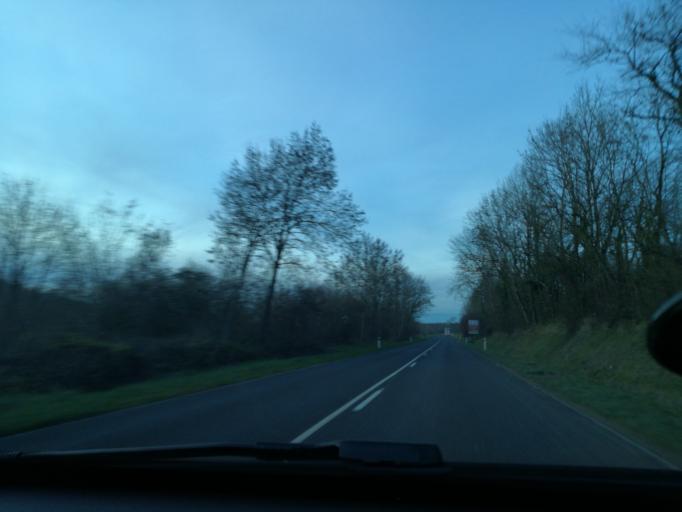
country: FR
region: Lorraine
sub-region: Departement de la Meuse
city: Fains-Veel
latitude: 48.7991
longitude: 5.1211
